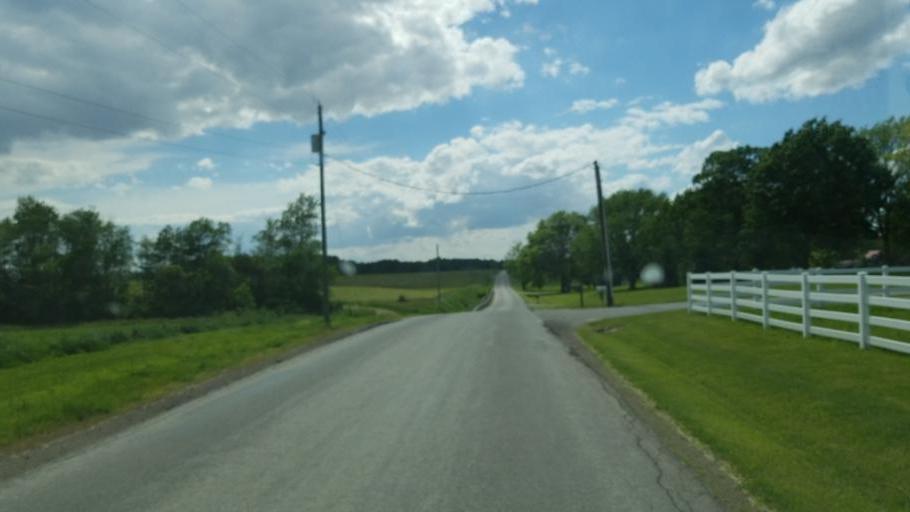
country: US
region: Ohio
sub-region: Huron County
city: Plymouth
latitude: 40.9697
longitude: -82.6359
